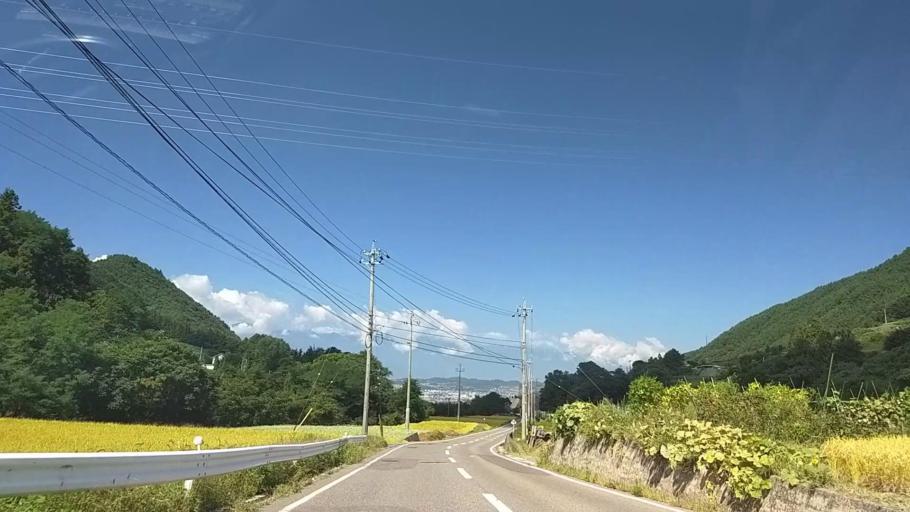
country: JP
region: Nagano
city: Matsumoto
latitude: 36.2233
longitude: 138.0362
